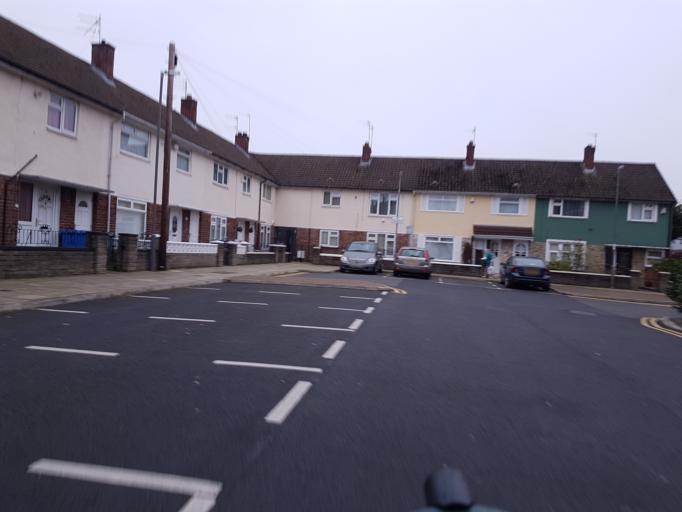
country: GB
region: England
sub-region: Liverpool
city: Liverpool
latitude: 53.4369
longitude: -2.9743
